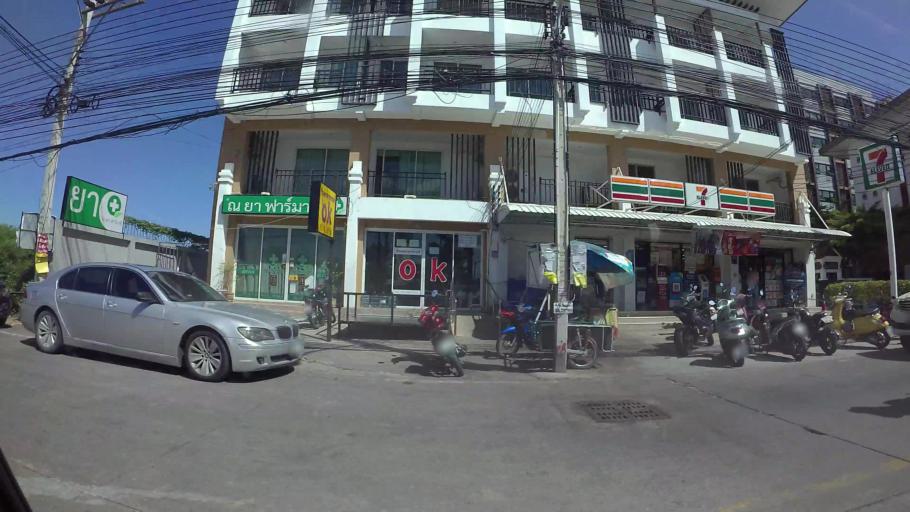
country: TH
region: Chon Buri
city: Phatthaya
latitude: 12.9454
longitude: 100.9016
